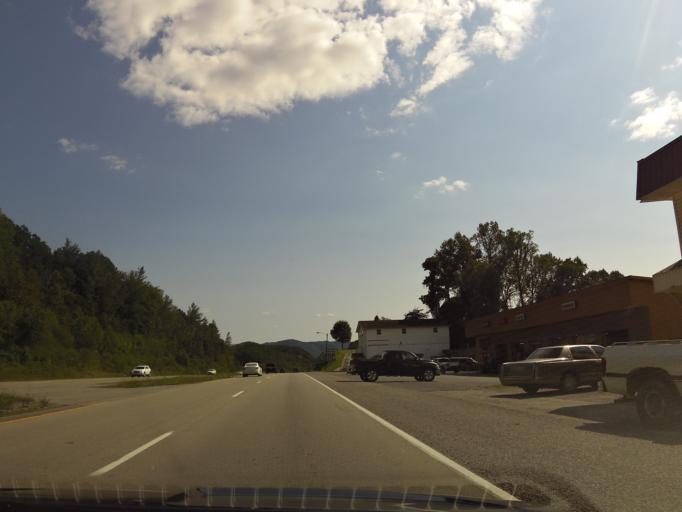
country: US
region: Kentucky
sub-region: Bell County
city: Middlesboro
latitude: 36.6368
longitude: -83.7041
